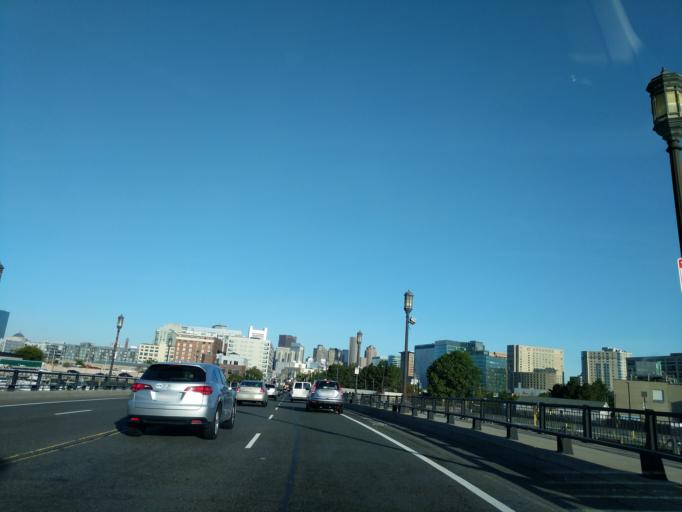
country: US
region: Massachusetts
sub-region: Suffolk County
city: South Boston
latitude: 42.3425
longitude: -71.0362
